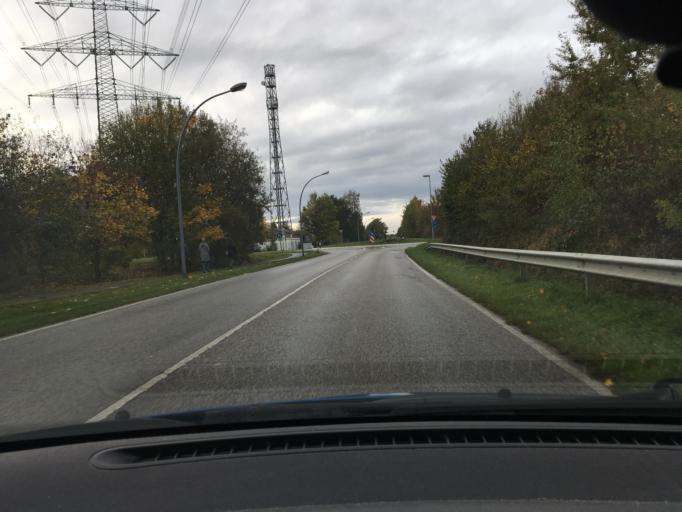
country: DE
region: Schleswig-Holstein
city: Bornsen
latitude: 53.4870
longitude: 10.2897
